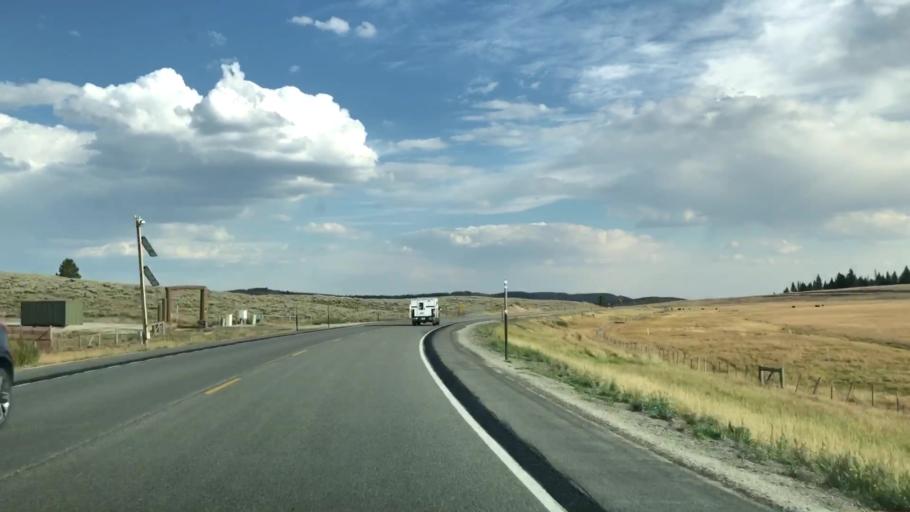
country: US
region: Wyoming
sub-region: Sublette County
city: Pinedale
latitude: 43.1307
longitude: -110.1922
